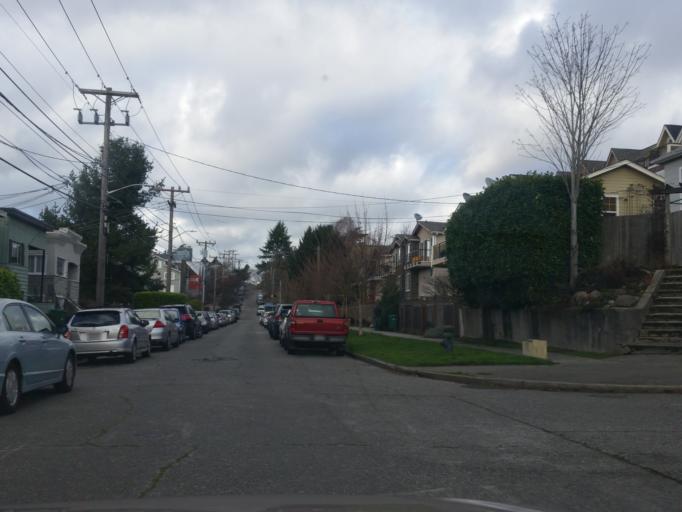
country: US
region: Washington
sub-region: King County
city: Seattle
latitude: 47.6589
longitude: -122.3555
